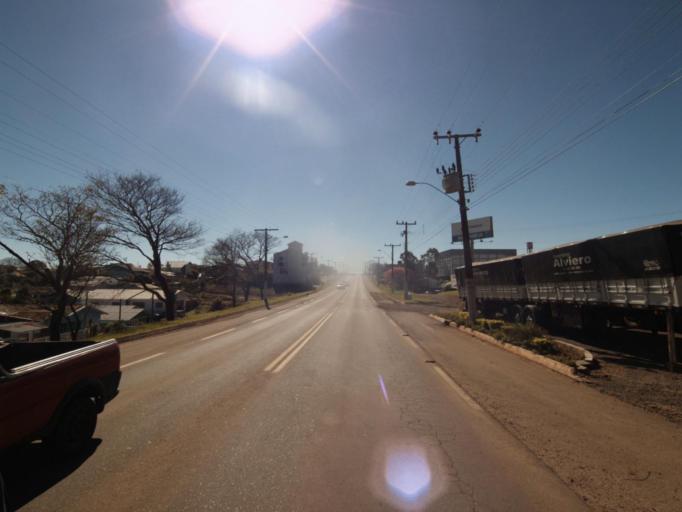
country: AR
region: Misiones
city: Bernardo de Irigoyen
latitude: -26.7438
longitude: -53.5188
